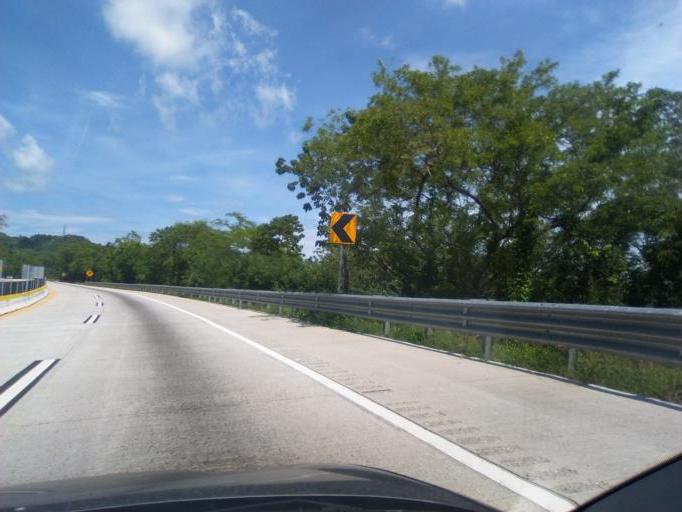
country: MX
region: Guerrero
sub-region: Acapulco de Juarez
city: Kilometro 30
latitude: 16.9460
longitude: -99.7652
